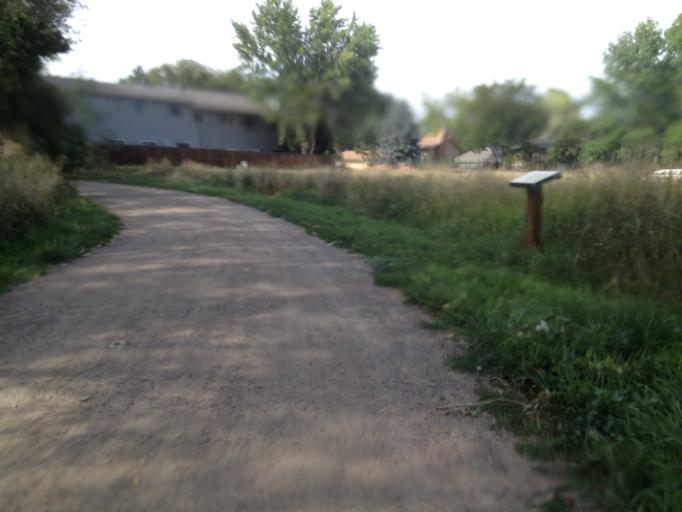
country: US
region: Colorado
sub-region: Boulder County
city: Louisville
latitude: 39.9789
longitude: -105.1117
